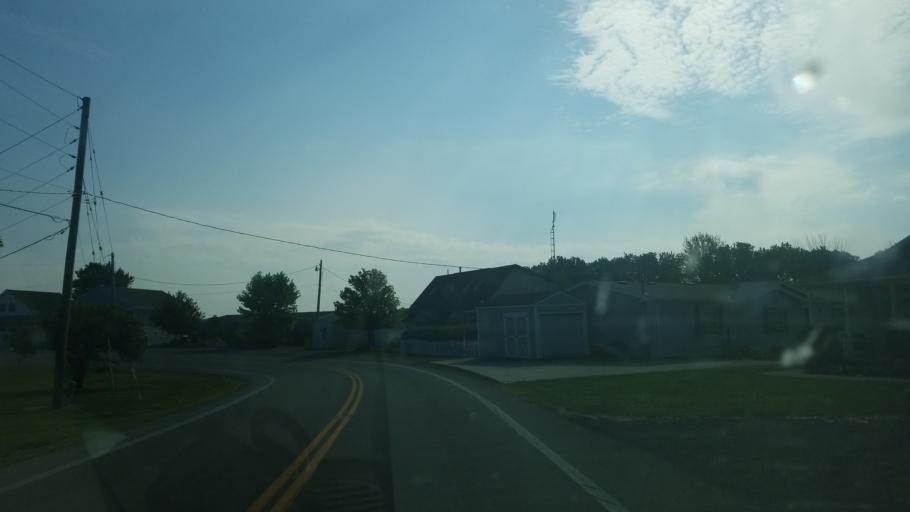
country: US
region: Ohio
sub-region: Logan County
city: Russells Point
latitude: 40.4871
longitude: -83.8613
